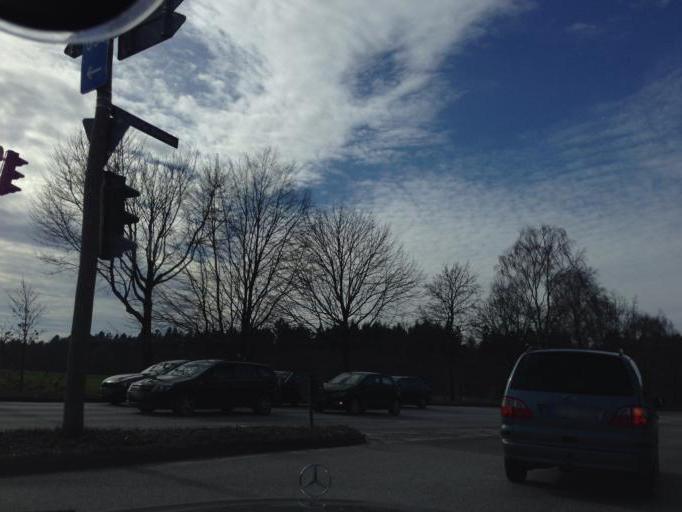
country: DE
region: Lower Saxony
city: Seevetal
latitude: 53.4313
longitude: 9.9323
